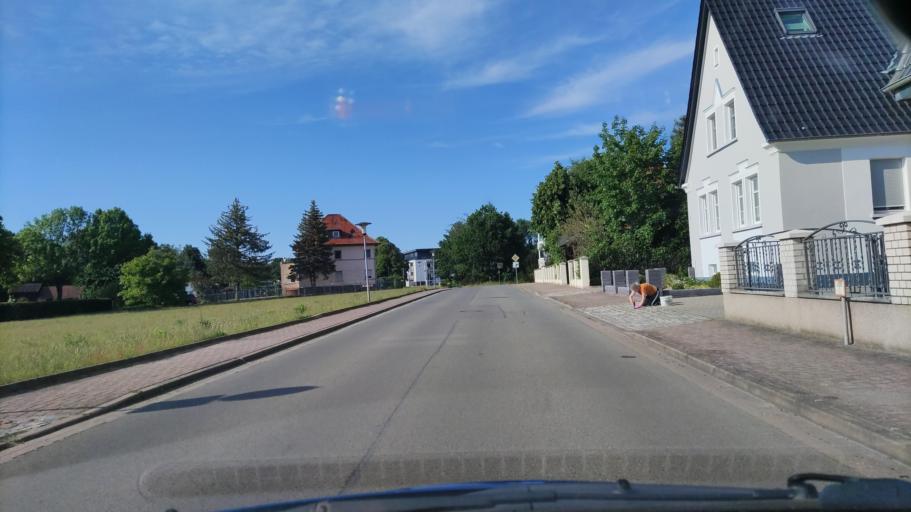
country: DE
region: Saxony-Anhalt
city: Gardelegen
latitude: 52.5300
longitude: 11.3883
